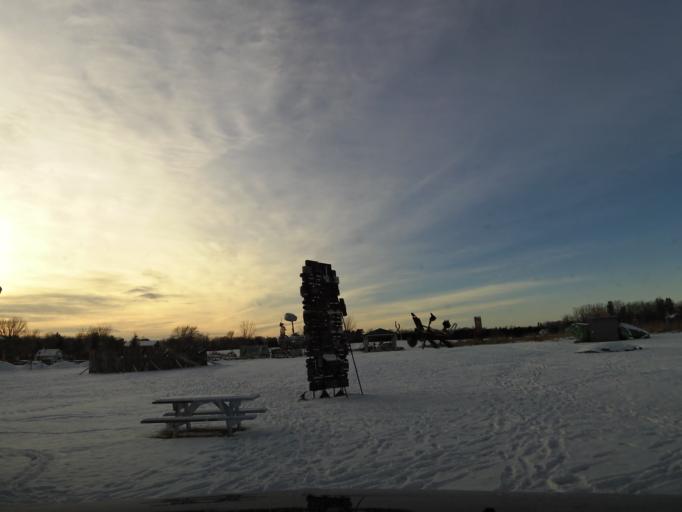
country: US
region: Minnesota
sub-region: Chisago County
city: Shafer
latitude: 45.3804
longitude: -92.7042
